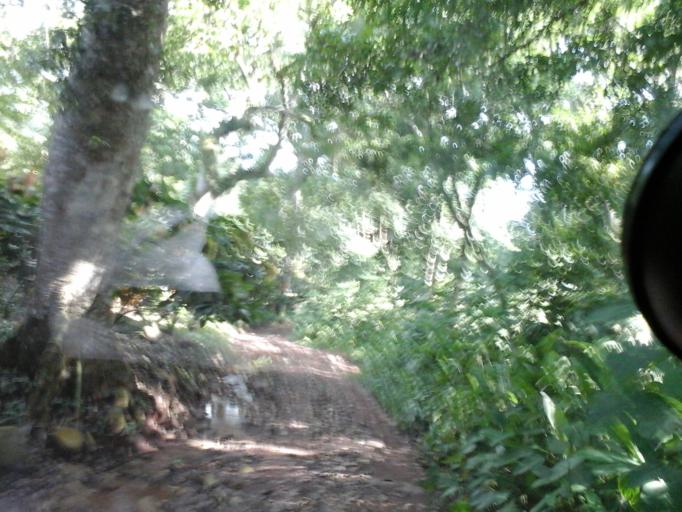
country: CO
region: Cesar
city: San Diego
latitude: 10.2775
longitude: -73.0938
